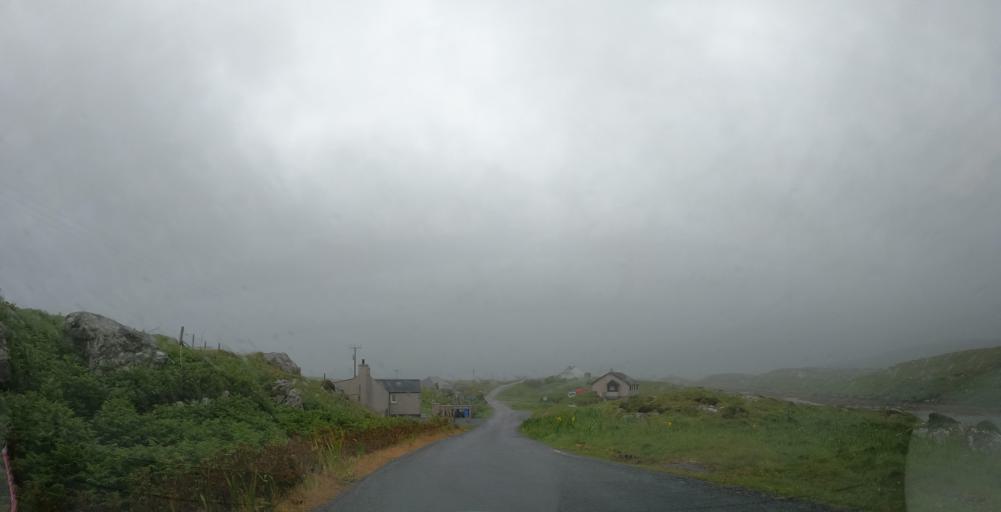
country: GB
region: Scotland
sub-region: Eilean Siar
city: Barra
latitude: 57.0121
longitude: -7.4275
